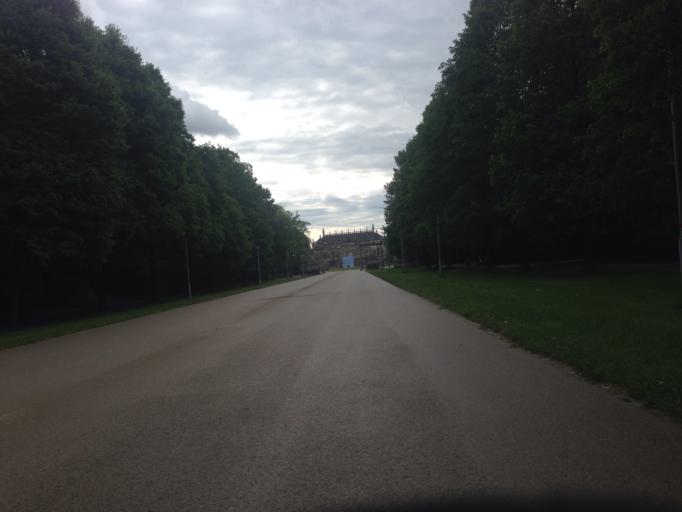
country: DE
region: Saxony
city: Dresden
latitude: 51.0398
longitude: 13.7579
